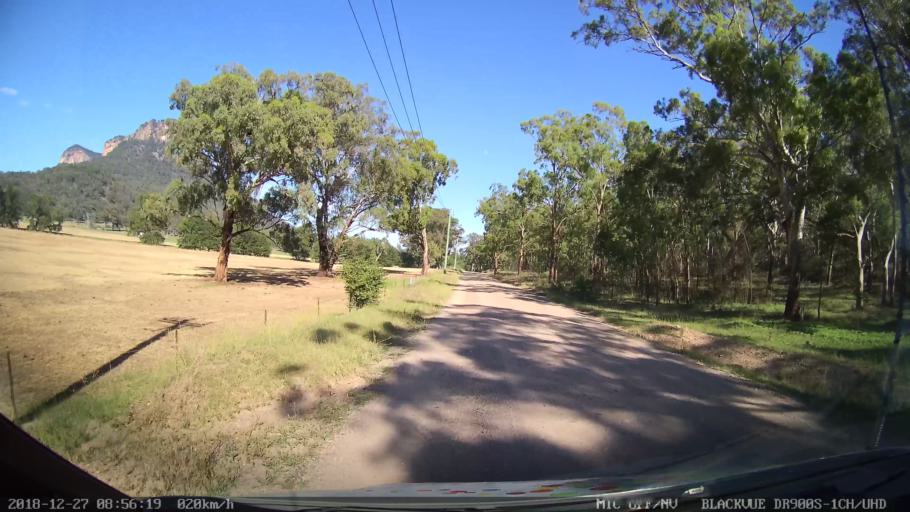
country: AU
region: New South Wales
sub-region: Lithgow
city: Portland
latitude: -33.1107
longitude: 150.2524
